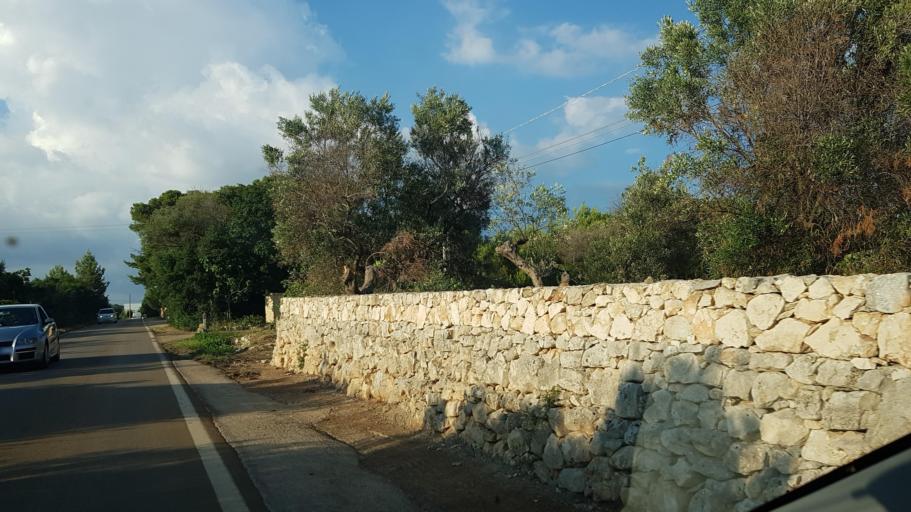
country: IT
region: Apulia
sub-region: Provincia di Lecce
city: Gemini
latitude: 39.8484
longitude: 18.2080
